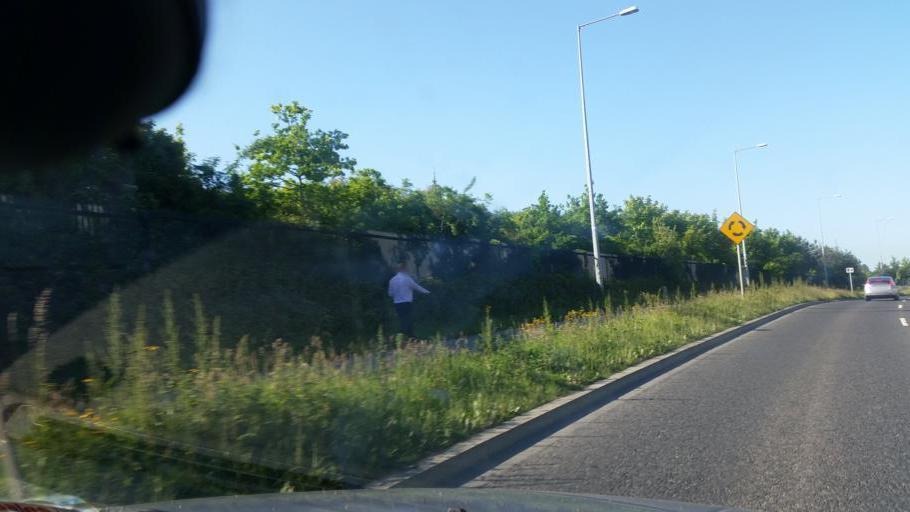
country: IE
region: Leinster
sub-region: Fingal County
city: Blanchardstown
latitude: 53.4174
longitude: -6.3824
